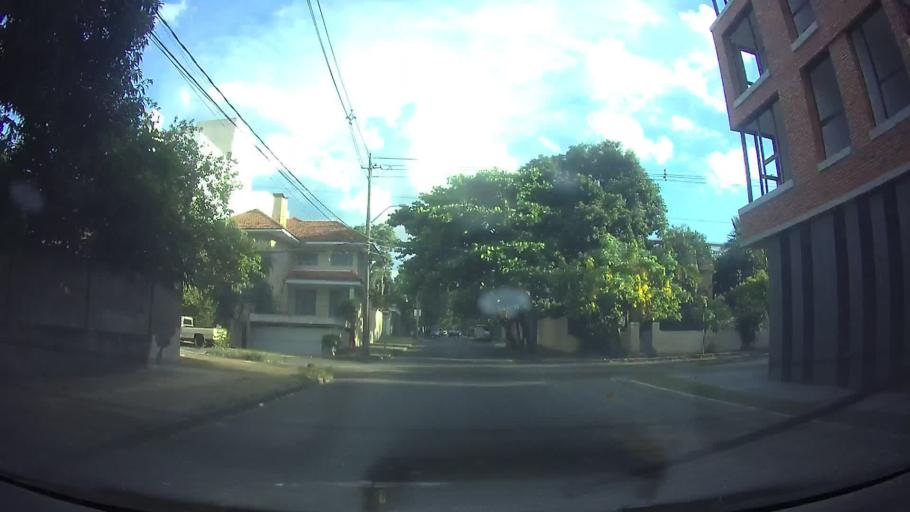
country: PY
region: Asuncion
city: Asuncion
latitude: -25.2776
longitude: -57.6039
